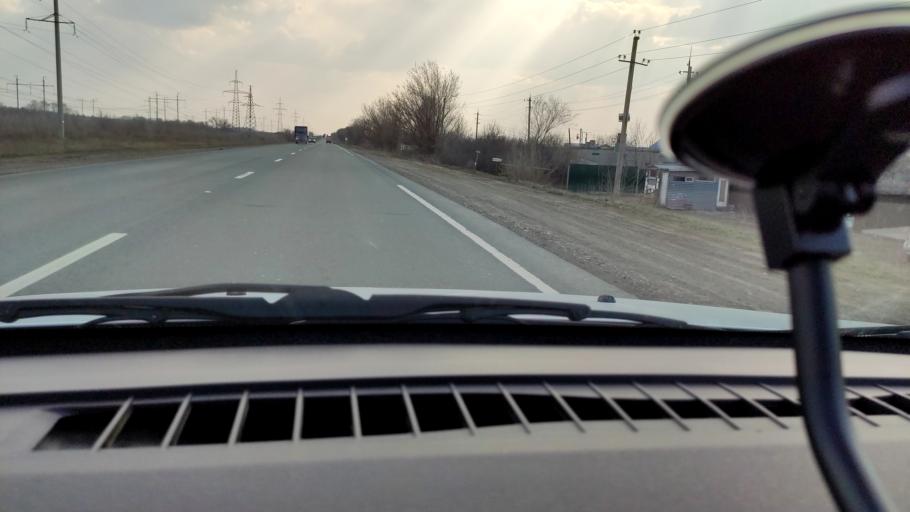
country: RU
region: Samara
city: Smyshlyayevka
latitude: 53.0864
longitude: 50.3939
